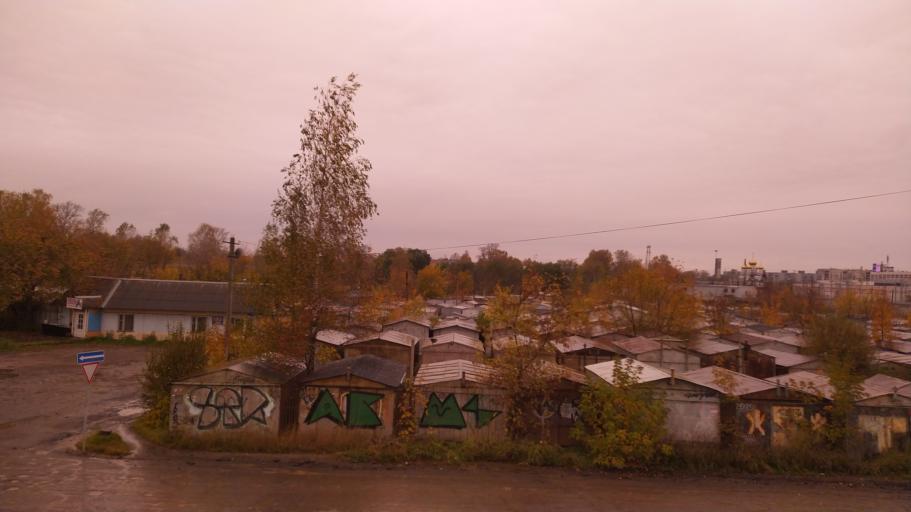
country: RU
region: Tverskaya
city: Tver
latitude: 56.8305
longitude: 35.9001
